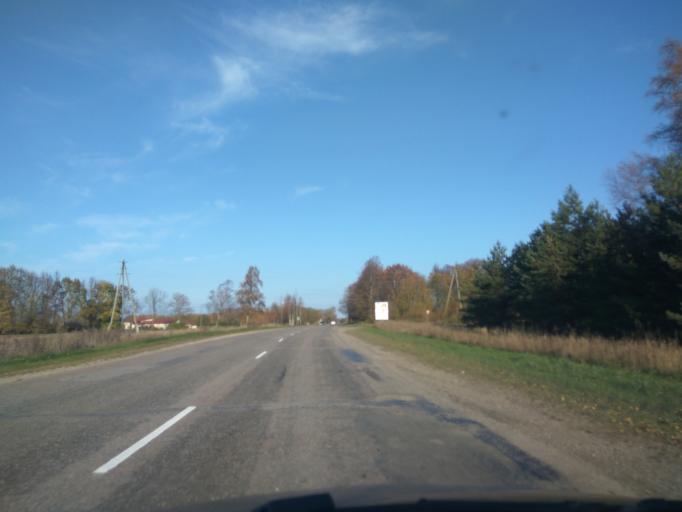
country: LV
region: Ventspils
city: Ventspils
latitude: 57.3154
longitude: 21.5573
